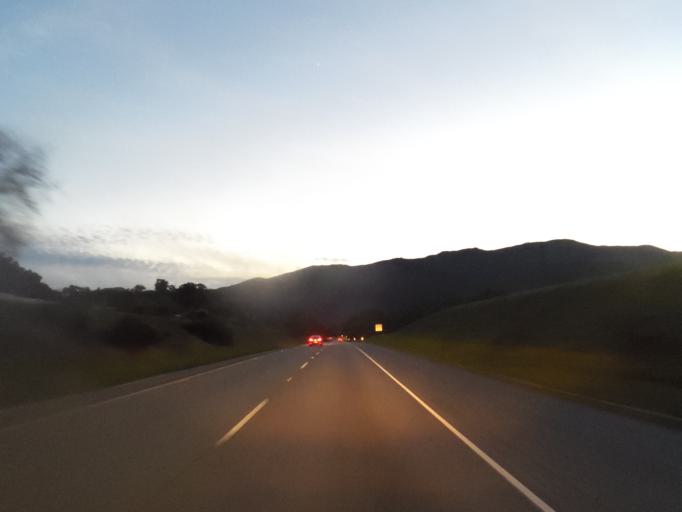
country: US
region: California
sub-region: San Luis Obispo County
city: Santa Margarita
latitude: 35.3759
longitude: -120.6372
